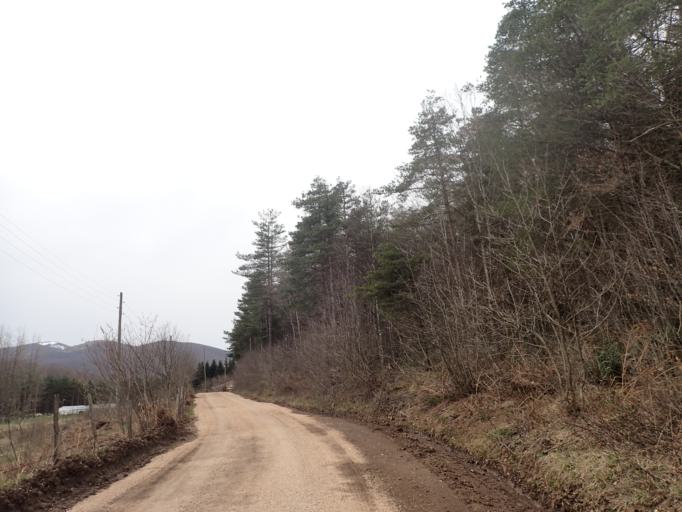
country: TR
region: Ordu
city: Kumru
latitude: 40.8101
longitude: 37.1627
